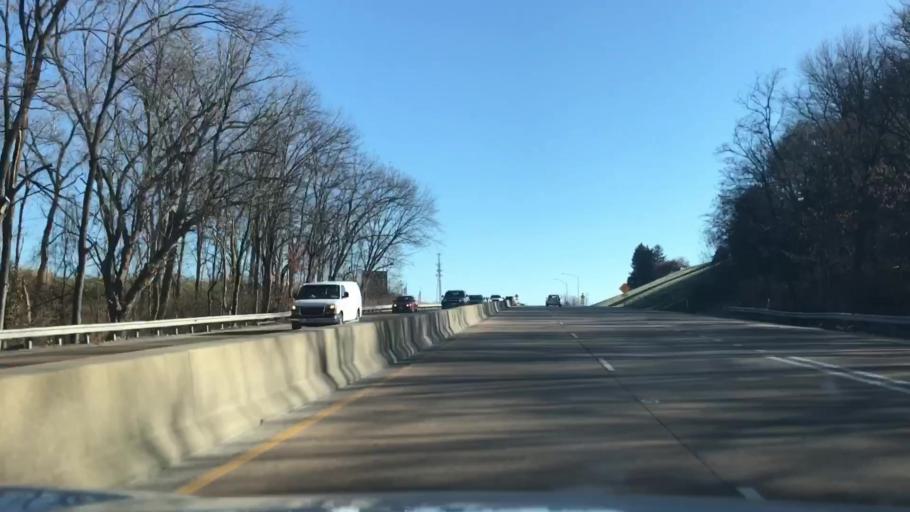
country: US
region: Illinois
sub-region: Saint Clair County
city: Alorton
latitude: 38.5648
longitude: -90.0884
